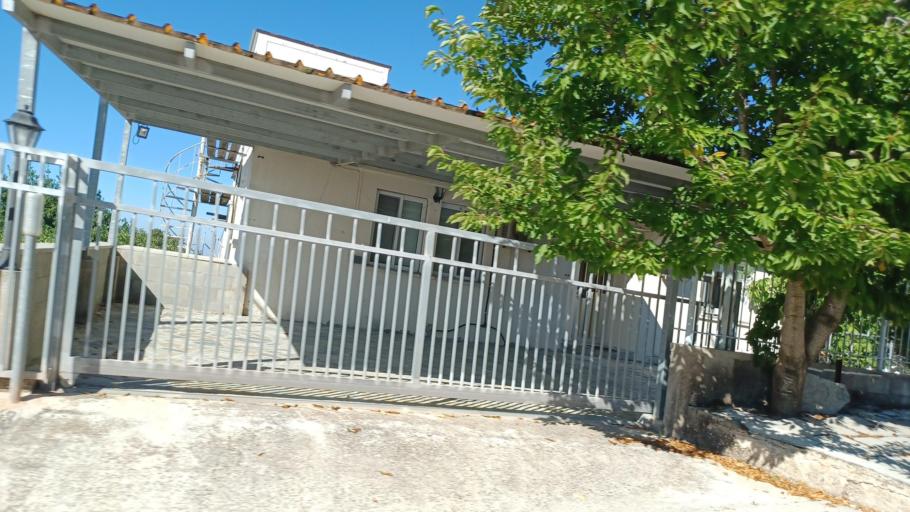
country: CY
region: Pafos
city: Mesogi
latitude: 34.8875
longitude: 32.6243
